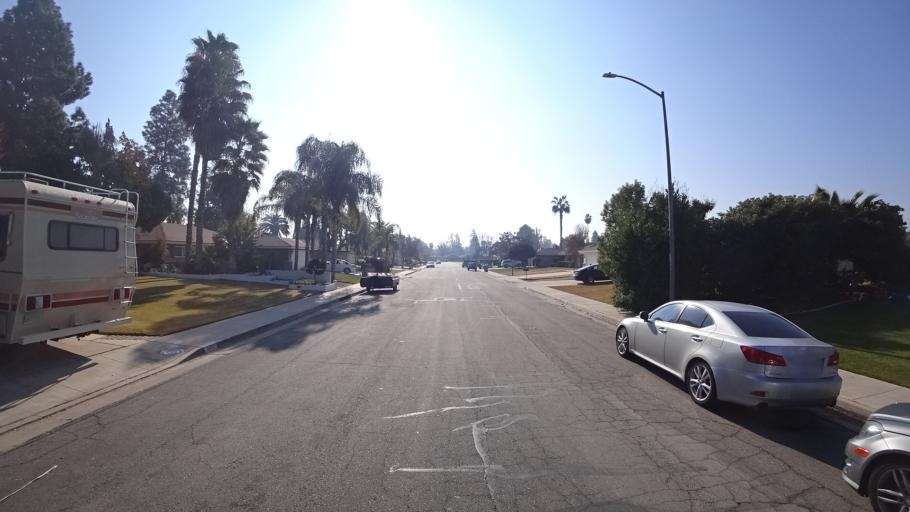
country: US
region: California
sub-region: Kern County
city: Greenacres
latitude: 35.3583
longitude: -119.0750
